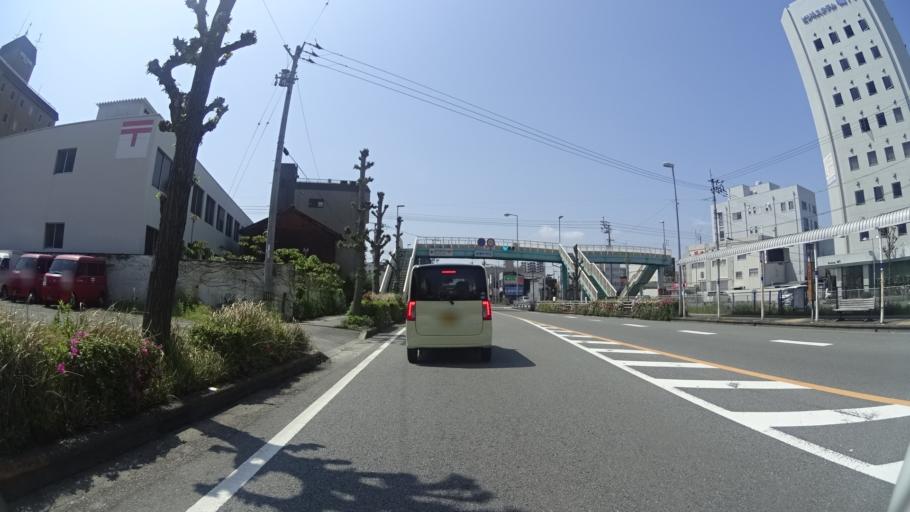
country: JP
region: Tokushima
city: Narutocho-mitsuishi
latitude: 34.1772
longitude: 134.6087
